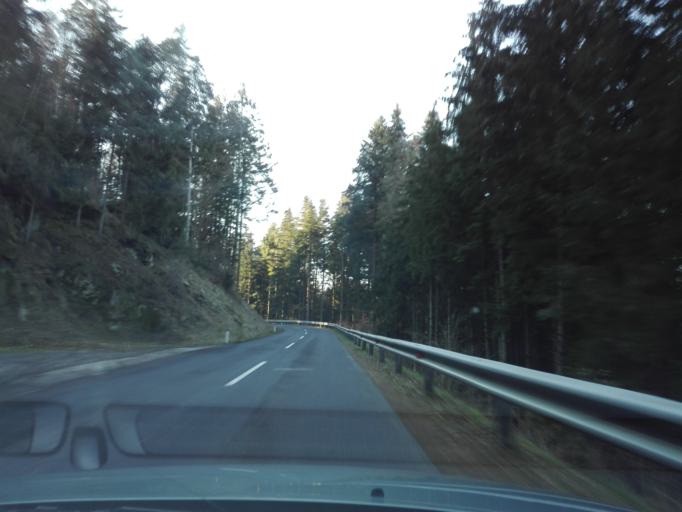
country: AT
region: Upper Austria
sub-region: Politischer Bezirk Rohrbach
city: Kleinzell im Muehlkreis
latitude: 48.4011
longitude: 13.9330
